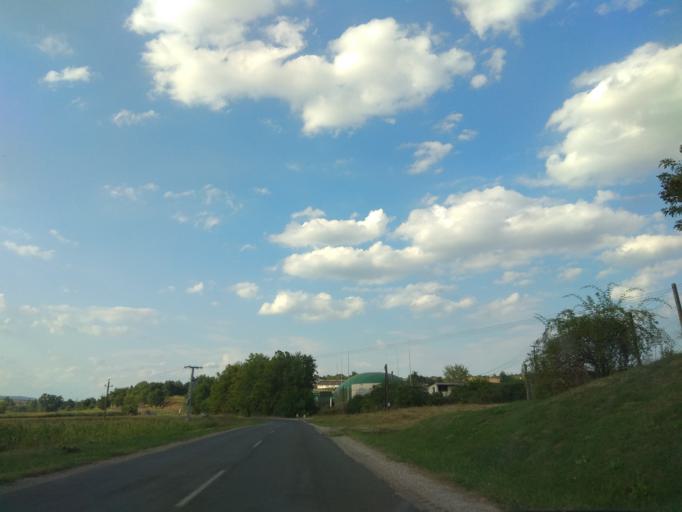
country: HU
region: Borsod-Abauj-Zemplen
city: Harsany
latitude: 47.9509
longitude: 20.7451
